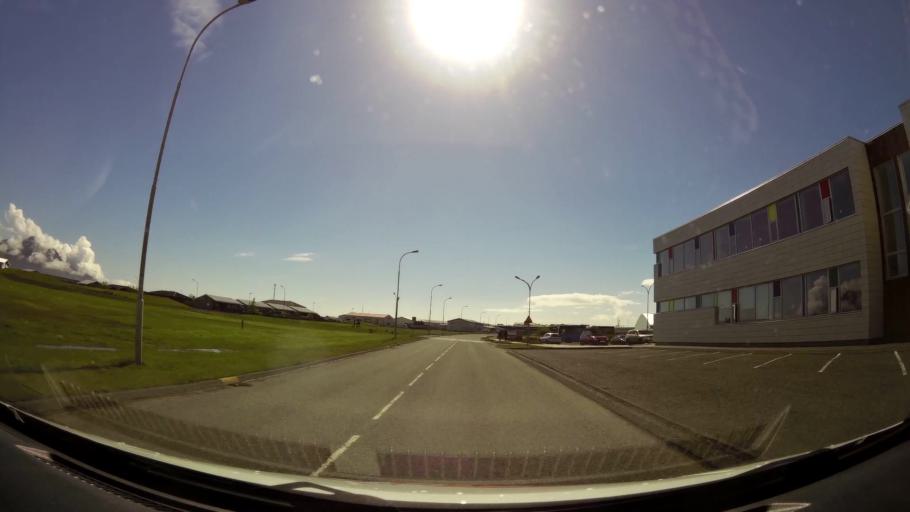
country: IS
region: East
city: Hoefn
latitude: 64.2544
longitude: -15.2068
